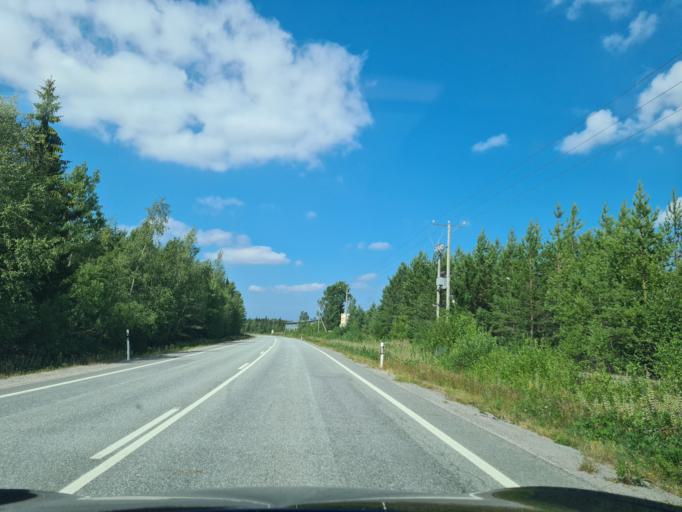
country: FI
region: Ostrobothnia
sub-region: Vaasa
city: Vaasa
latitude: 63.1658
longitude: 21.5894
